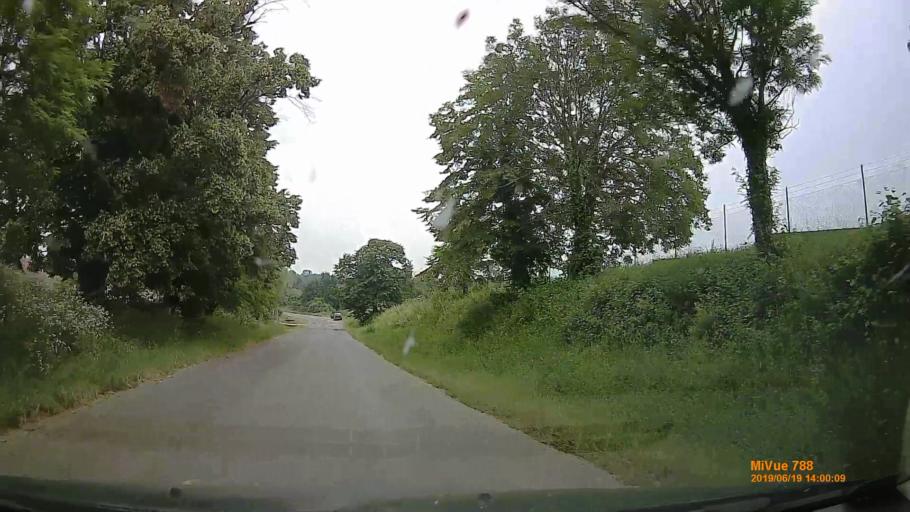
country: HU
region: Baranya
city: Szigetvar
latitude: 46.0854
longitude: 17.8012
